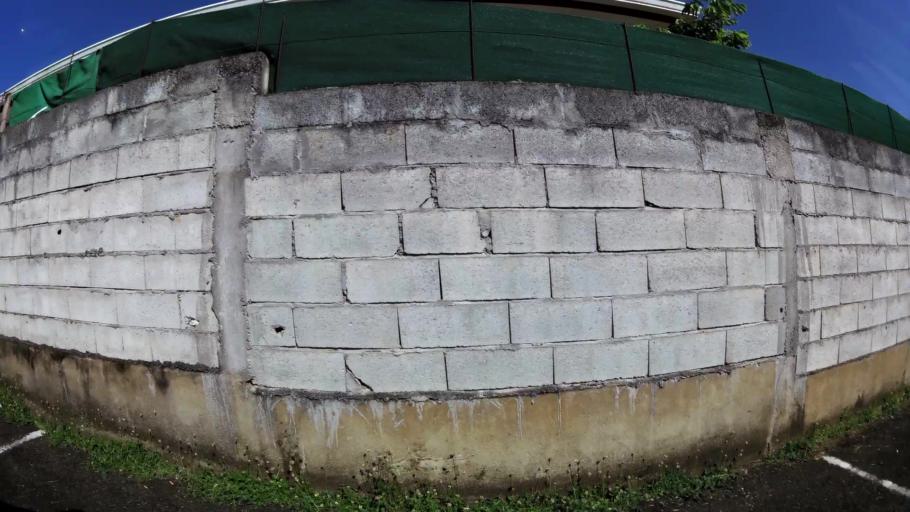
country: GF
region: Guyane
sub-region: Guyane
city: Remire-Montjoly
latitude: 4.9097
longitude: -52.2752
